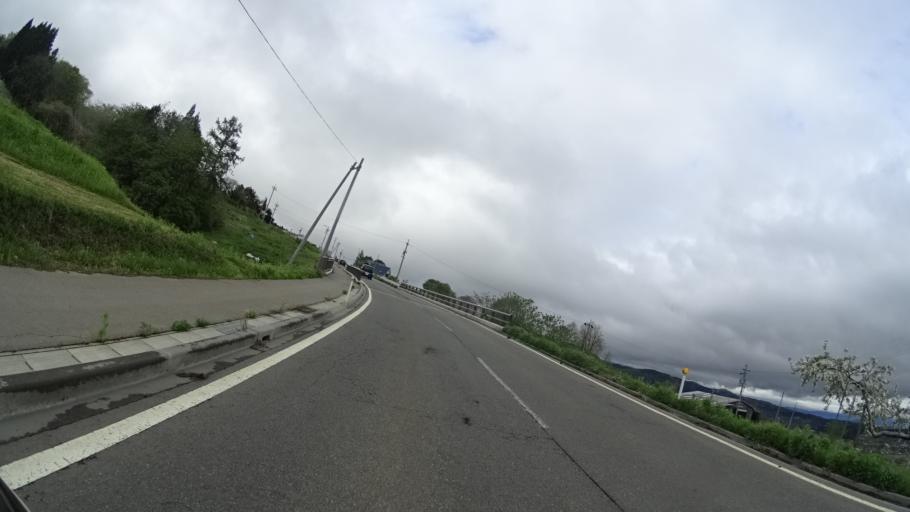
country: JP
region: Nagano
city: Nagano-shi
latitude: 36.7402
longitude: 138.2057
